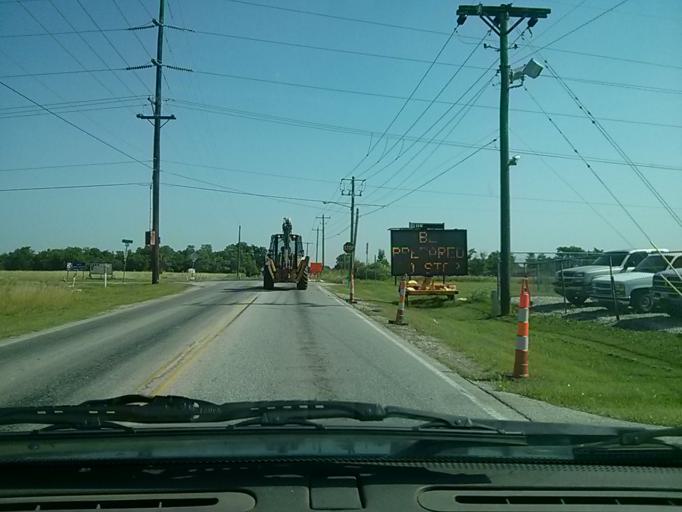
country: US
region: Oklahoma
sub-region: Rogers County
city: Catoosa
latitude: 36.1475
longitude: -95.7617
